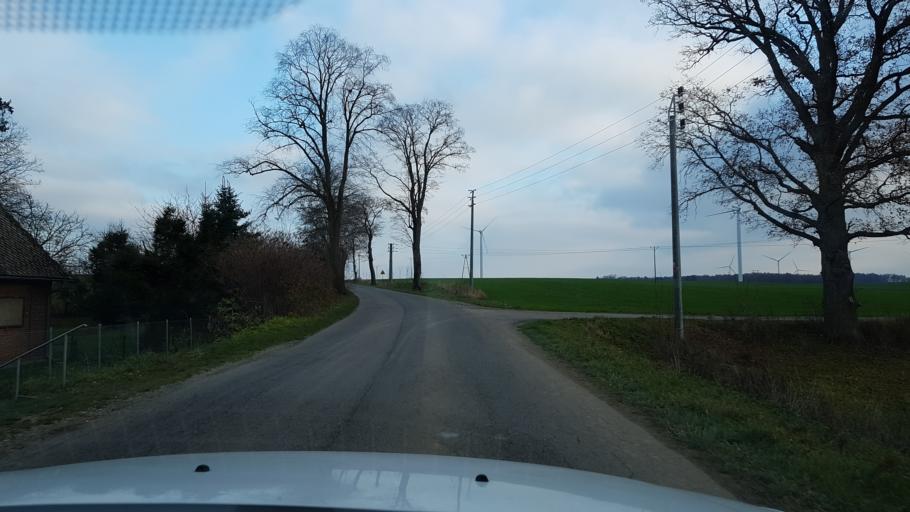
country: PL
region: West Pomeranian Voivodeship
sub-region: Powiat kolobrzeski
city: Goscino
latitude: 54.0544
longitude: 15.6866
